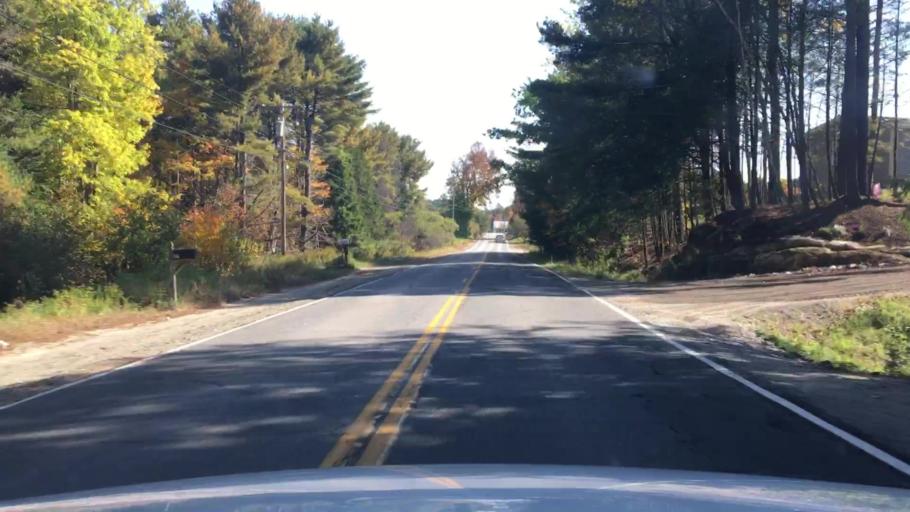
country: US
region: Maine
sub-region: Androscoggin County
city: Lisbon Falls
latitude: 44.0370
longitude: -69.9796
